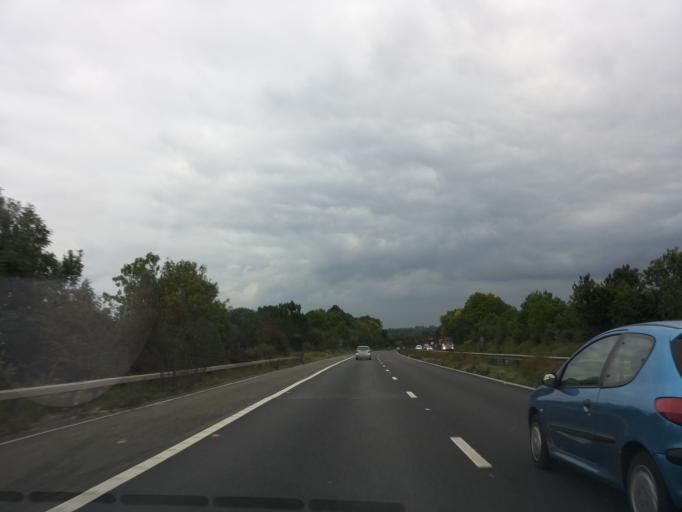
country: GB
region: England
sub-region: Kent
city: Rainham
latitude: 51.3422
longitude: 0.6223
